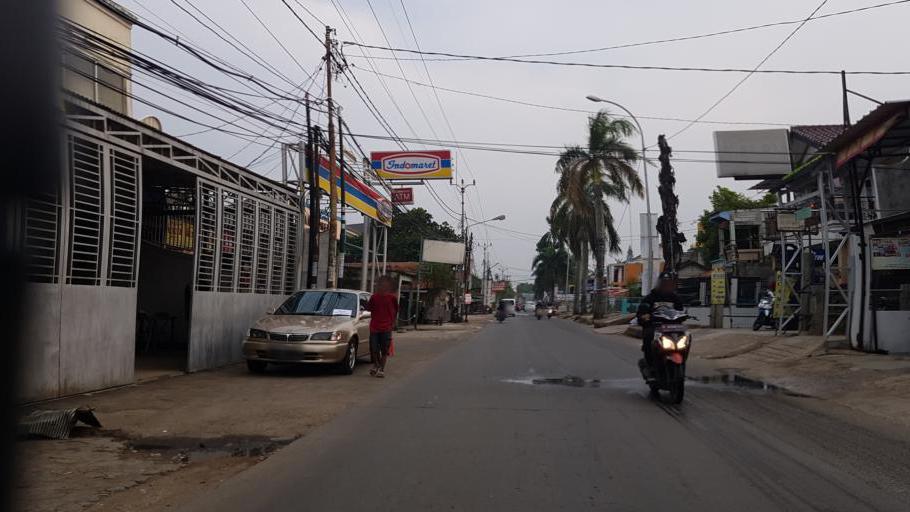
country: ID
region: West Java
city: Sawangan
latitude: -6.3911
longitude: 106.7947
